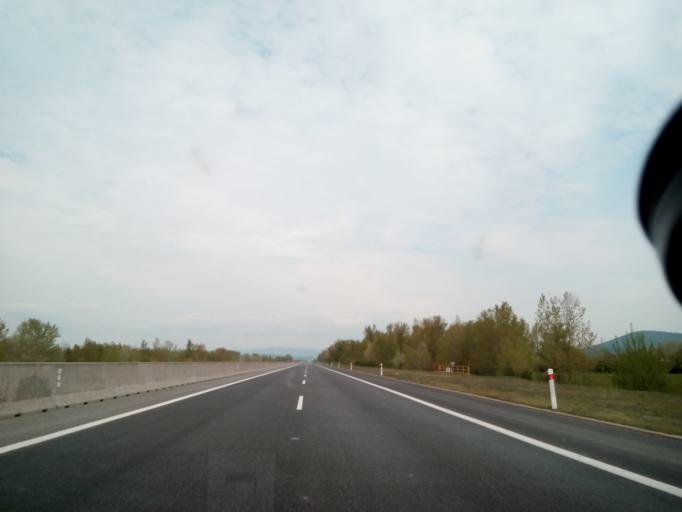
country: SK
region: Trenciansky
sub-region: Okres Nove Mesto nad Vahom
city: Nove Mesto nad Vahom
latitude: 48.6873
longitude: 17.8725
